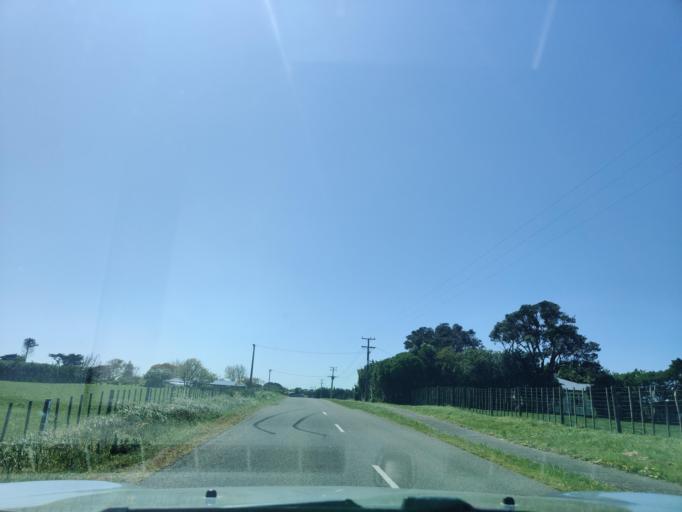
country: NZ
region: Taranaki
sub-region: South Taranaki District
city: Hawera
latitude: -39.5968
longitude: 174.2670
